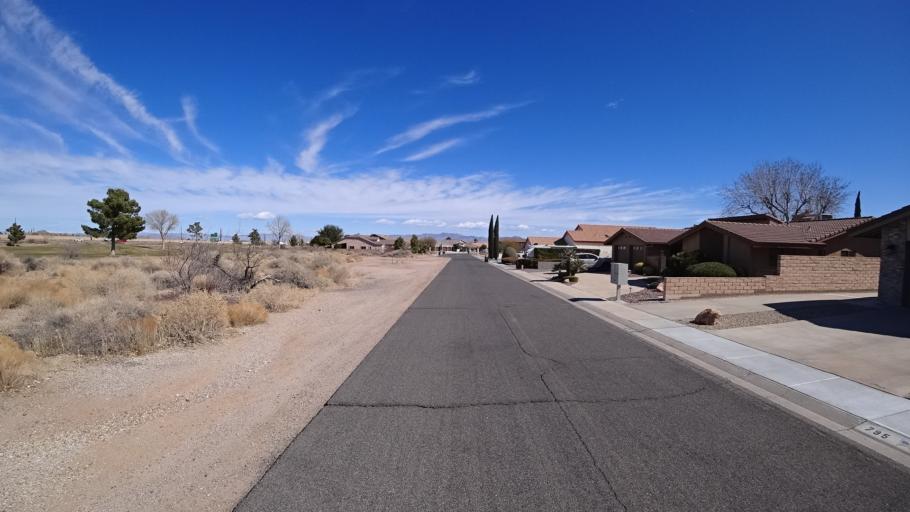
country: US
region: Arizona
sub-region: Mohave County
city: Kingman
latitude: 35.2126
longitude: -114.0477
